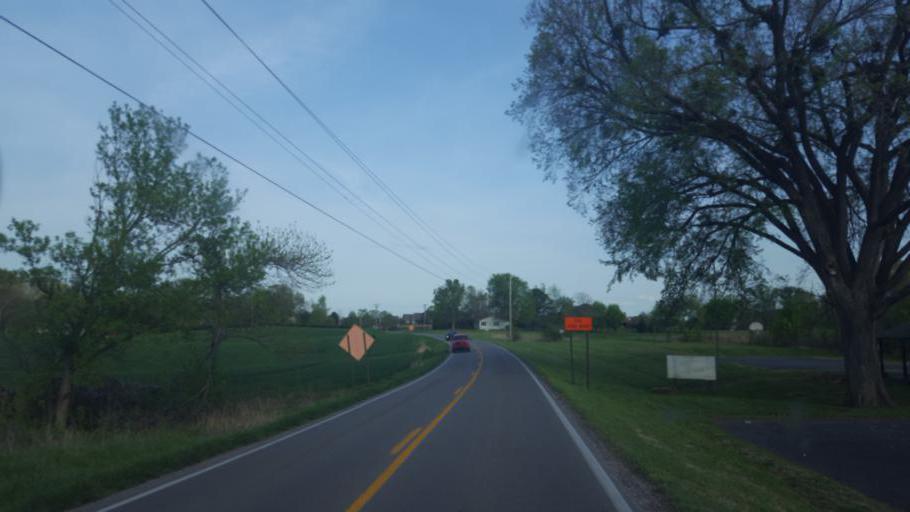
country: US
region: Kentucky
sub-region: Warren County
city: Bowling Green
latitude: 36.9656
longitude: -86.3751
